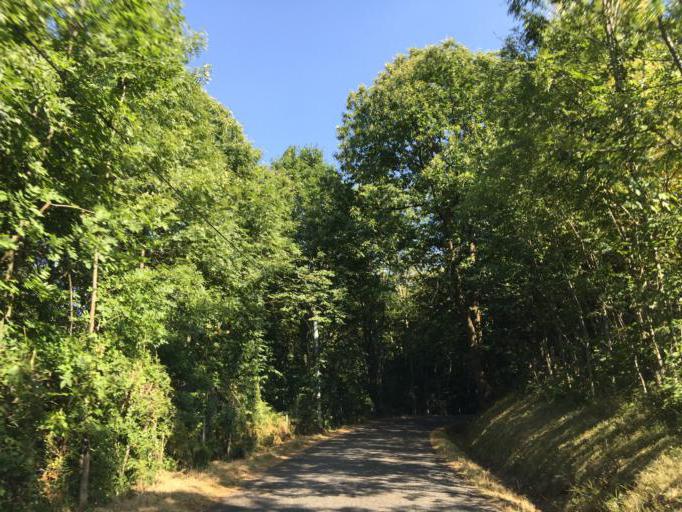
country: FR
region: Rhone-Alpes
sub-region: Departement de la Loire
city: Saint-Jean-Bonnefonds
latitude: 45.4321
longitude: 4.4732
